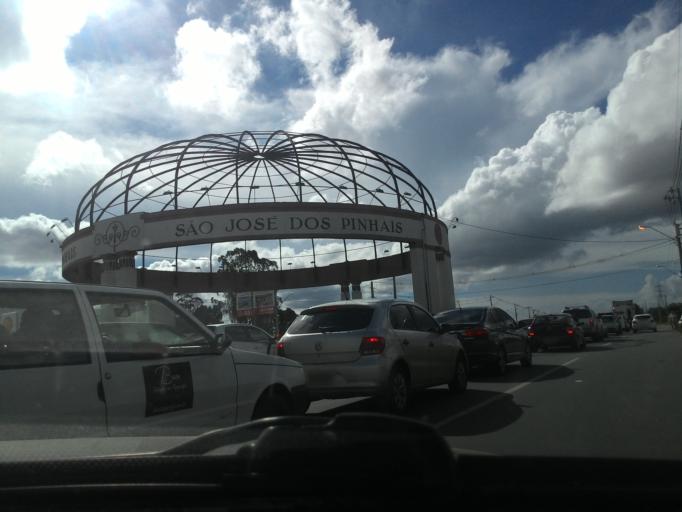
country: BR
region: Parana
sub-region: Sao Jose Dos Pinhais
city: Sao Jose dos Pinhais
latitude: -25.5145
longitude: -49.2012
